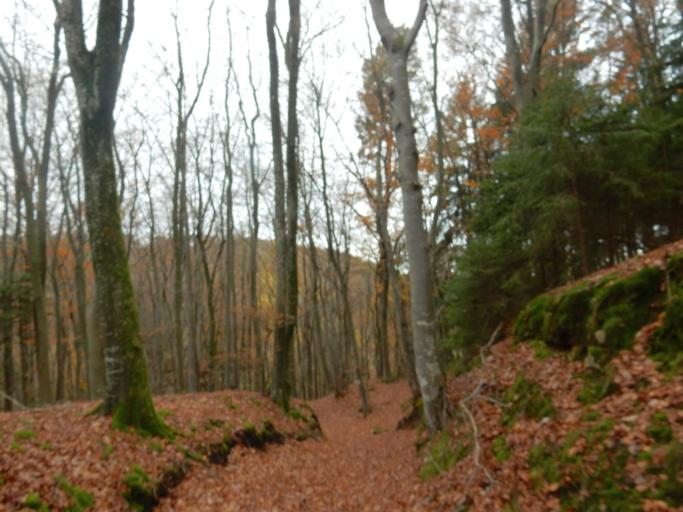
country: LU
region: Luxembourg
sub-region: Canton de Capellen
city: Septfontaines
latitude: 49.6980
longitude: 5.9883
